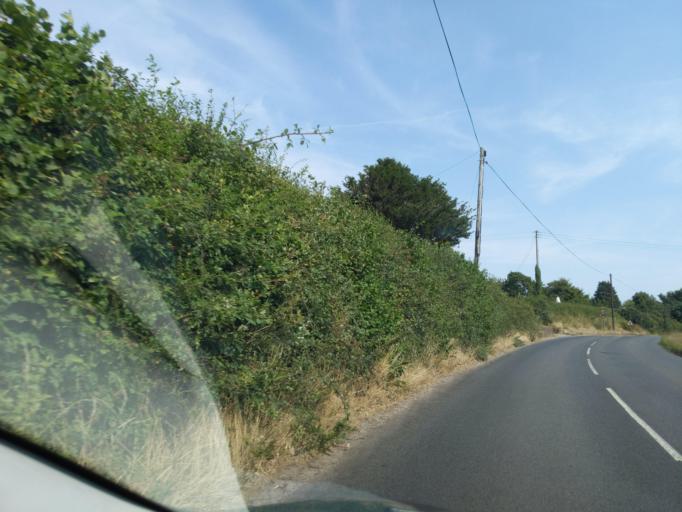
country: GB
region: England
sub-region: Devon
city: Winkleigh
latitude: 50.7935
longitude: -3.9536
